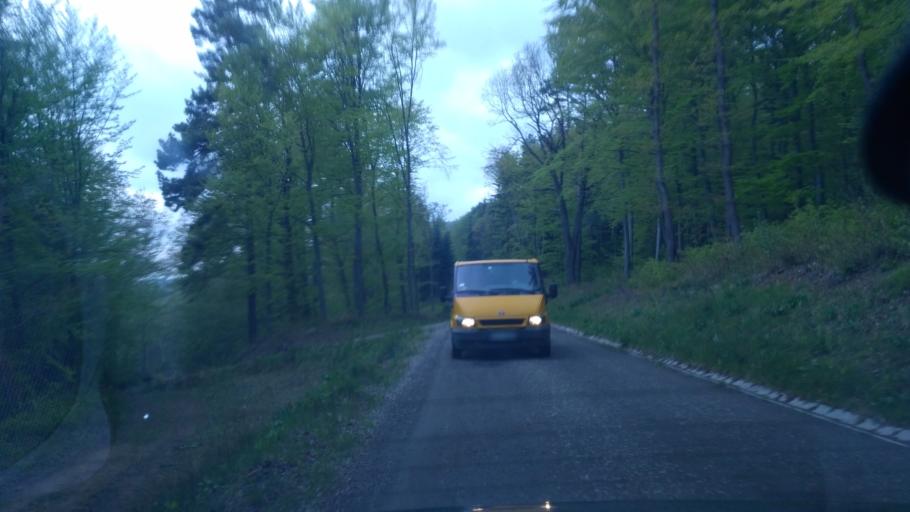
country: PL
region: Subcarpathian Voivodeship
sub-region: Powiat sanocki
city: Sanok
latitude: 49.5677
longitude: 22.2301
